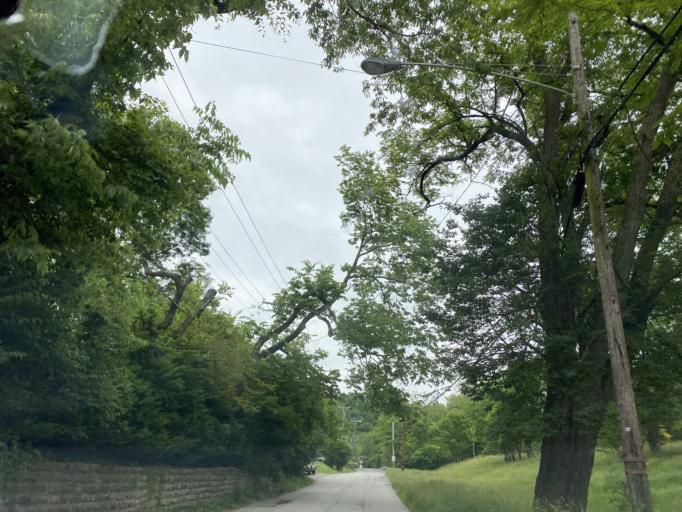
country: US
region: Kentucky
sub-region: Campbell County
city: Bellevue
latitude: 39.0995
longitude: -84.4676
